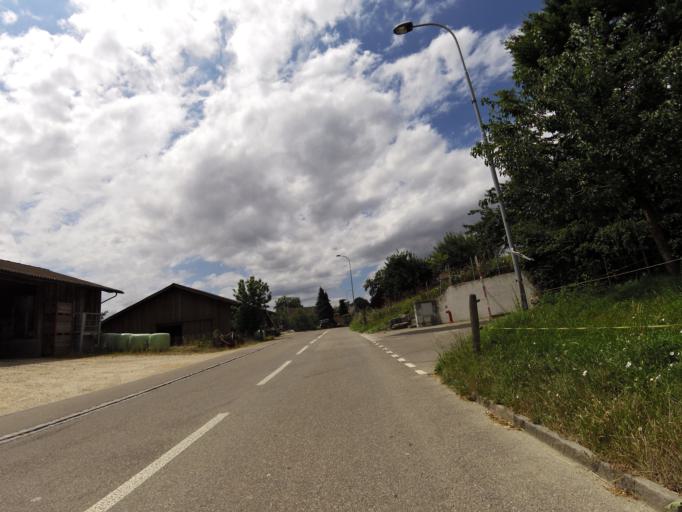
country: CH
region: Bern
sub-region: Oberaargau
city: Aarwangen
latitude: 47.2371
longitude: 7.7744
